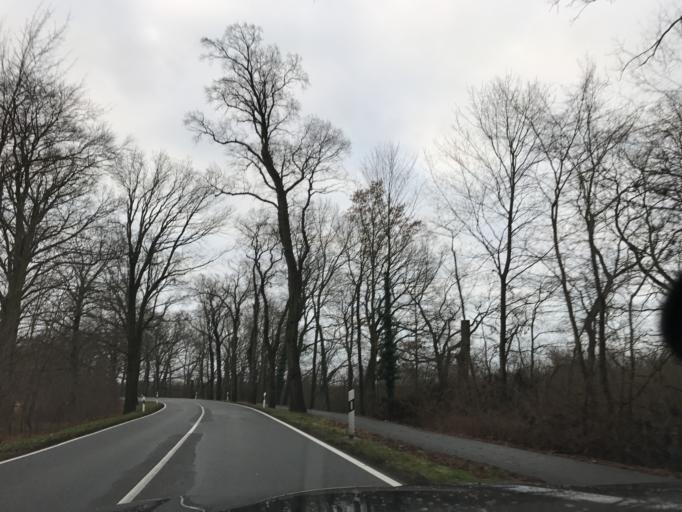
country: DE
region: Brandenburg
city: Werder
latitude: 52.3776
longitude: 12.9547
